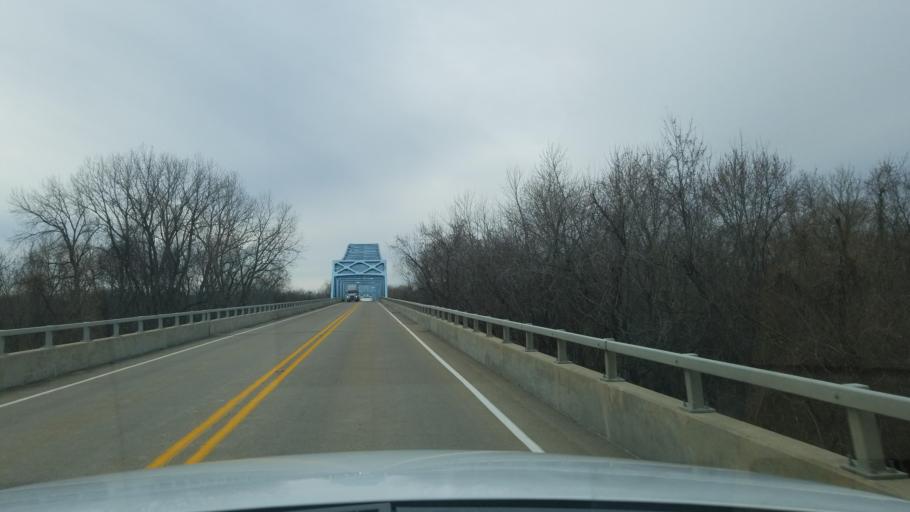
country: US
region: Indiana
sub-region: Posey County
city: Mount Vernon
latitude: 37.9440
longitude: -88.0327
